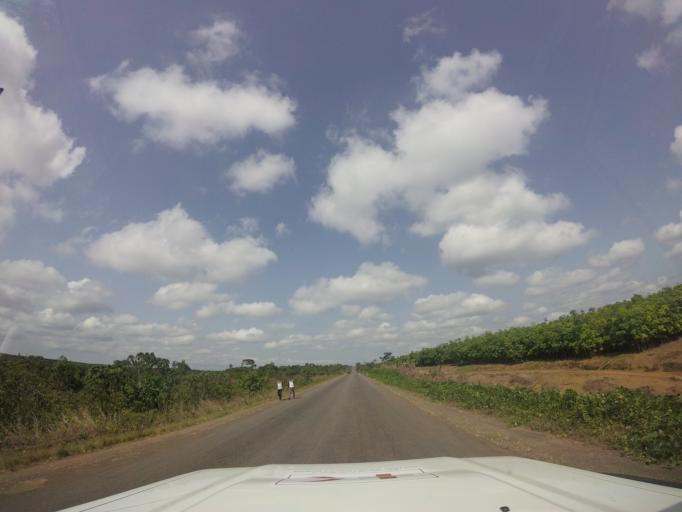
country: LR
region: Bomi
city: Tubmanburg
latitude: 6.7296
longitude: -11.0175
